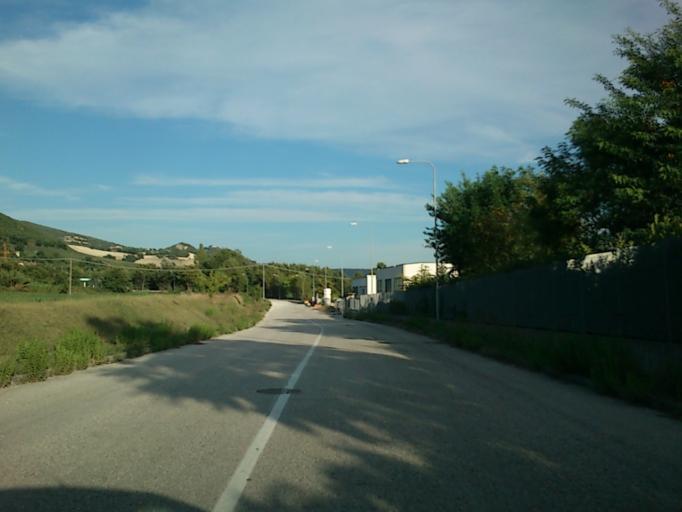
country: IT
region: The Marches
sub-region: Provincia di Pesaro e Urbino
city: Canavaccio
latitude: 43.6906
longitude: 12.7033
